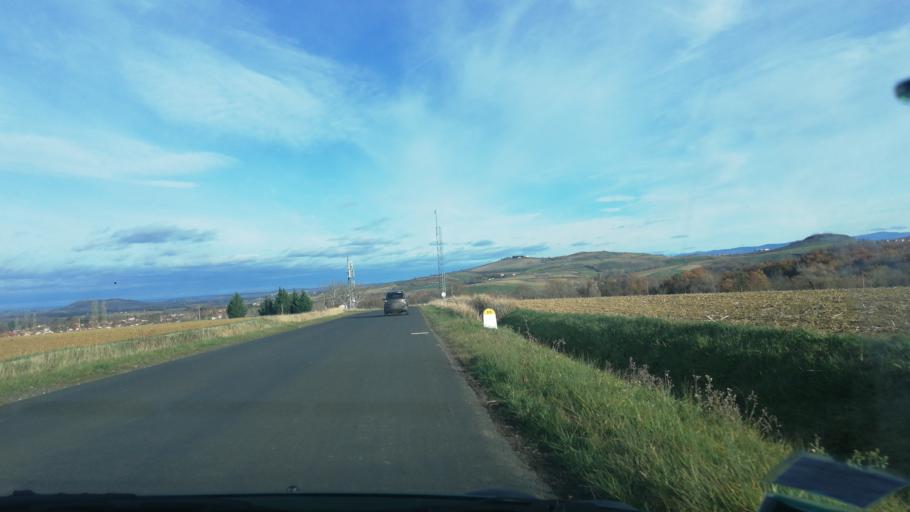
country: FR
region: Auvergne
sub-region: Departement du Puy-de-Dome
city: Billom
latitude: 45.7082
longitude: 3.3516
